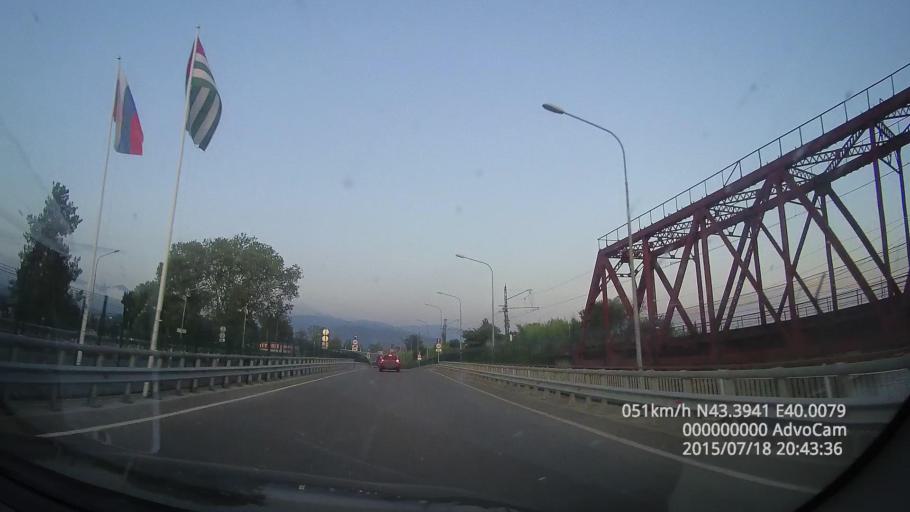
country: GE
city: Gantiadi
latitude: 43.3938
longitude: 40.0093
